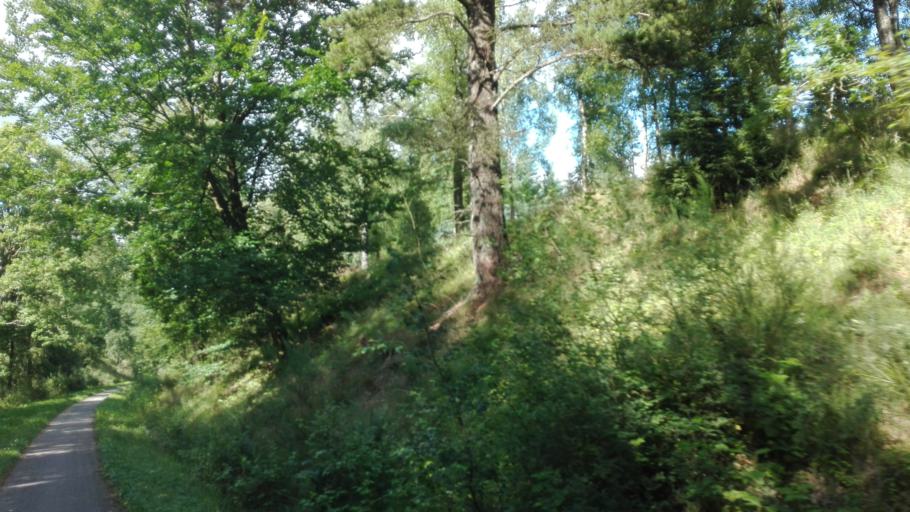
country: DK
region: Central Jutland
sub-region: Silkeborg Kommune
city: Virklund
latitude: 56.0575
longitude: 9.4713
